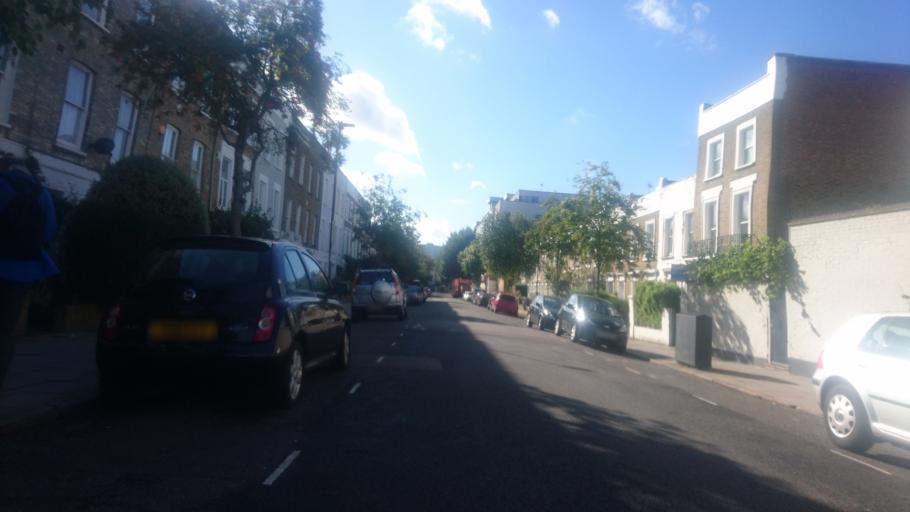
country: GB
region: England
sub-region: Greater London
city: Holloway
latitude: 51.5611
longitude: -0.1173
